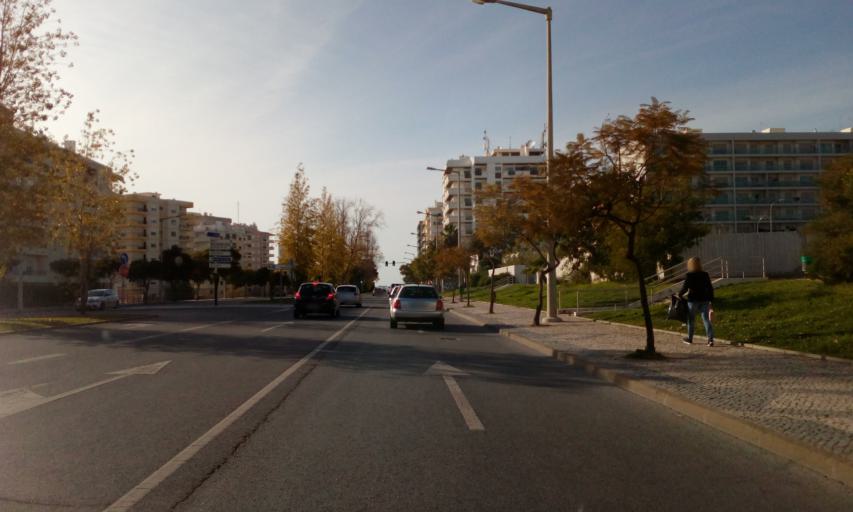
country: PT
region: Faro
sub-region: Faro
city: Faro
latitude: 37.0260
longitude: -7.9332
